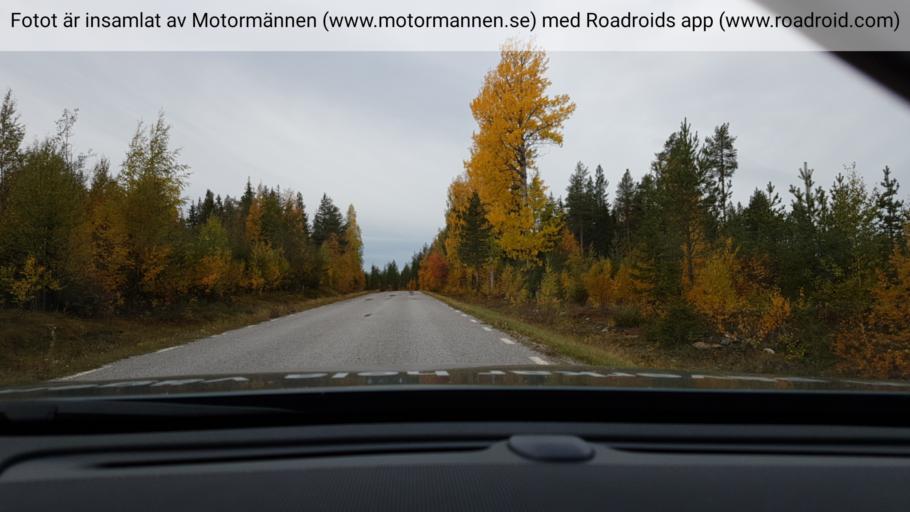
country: SE
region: Norrbotten
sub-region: Overkalix Kommun
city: OEverkalix
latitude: 66.2590
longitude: 23.0582
